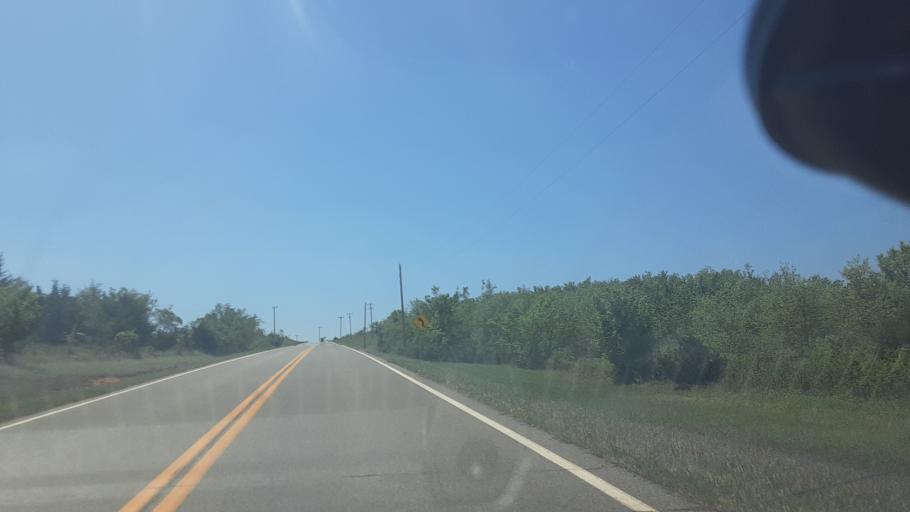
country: US
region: Oklahoma
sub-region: Logan County
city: Guthrie
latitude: 36.0459
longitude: -97.4072
